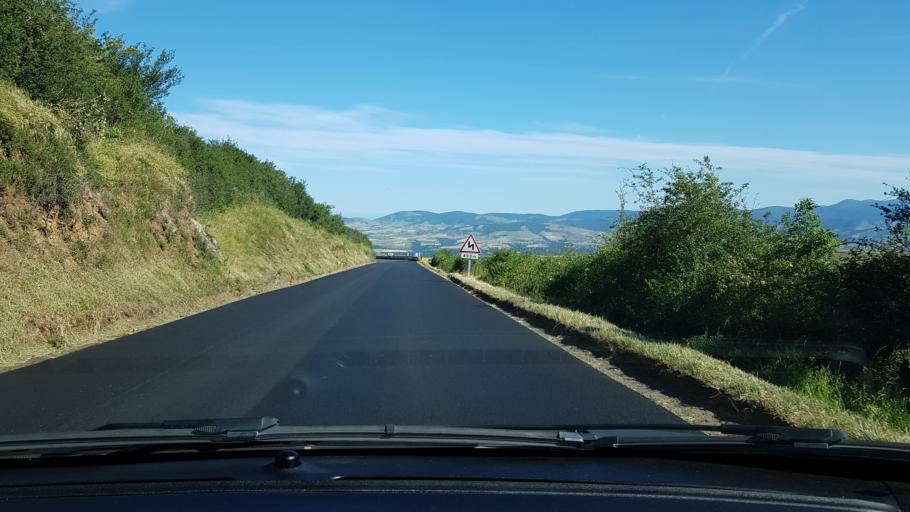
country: FR
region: Rhone-Alpes
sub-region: Departement du Rhone
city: Saint-Didier-sous-Riverie
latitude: 45.5959
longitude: 4.5879
